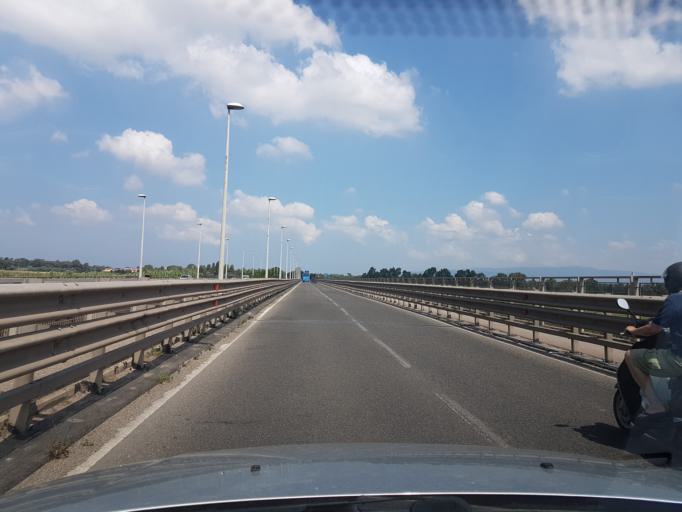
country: IT
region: Sardinia
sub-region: Provincia di Oristano
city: Donigala Fenugheddu
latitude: 39.9187
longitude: 8.5833
